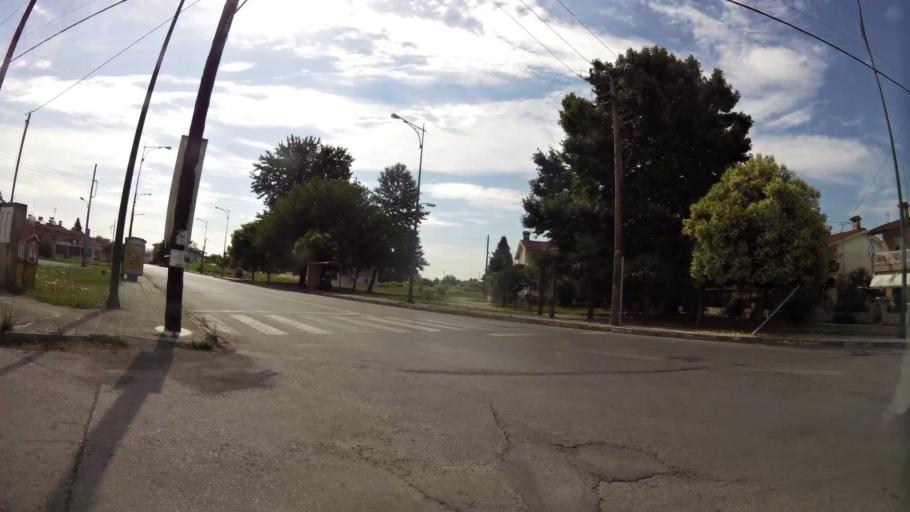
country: GR
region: Central Macedonia
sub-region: Nomos Pierias
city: Katerini
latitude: 40.2841
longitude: 22.5157
